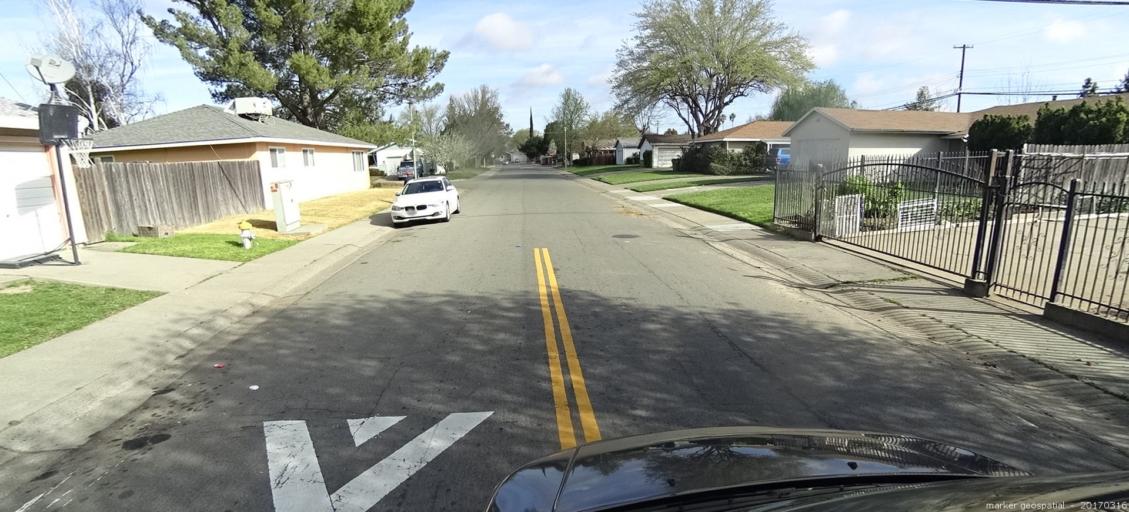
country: US
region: California
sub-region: Sacramento County
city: Parkway
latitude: 38.5055
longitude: -121.4836
